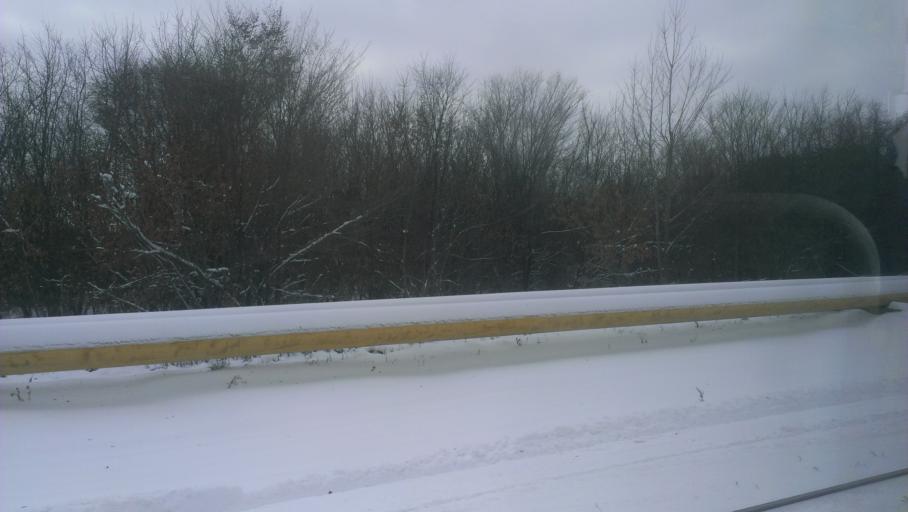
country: RU
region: Altai Krai
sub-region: Gorod Barnaulskiy
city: Barnaul
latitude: 53.3872
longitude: 83.6999
